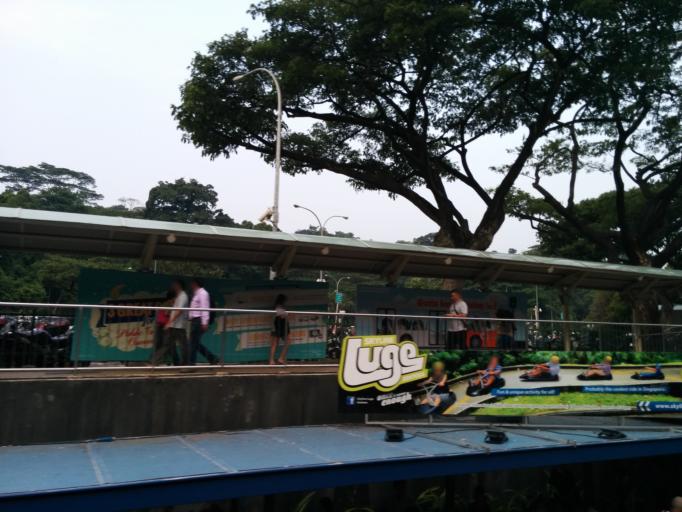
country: SG
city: Singapore
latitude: 1.2660
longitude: 103.8199
